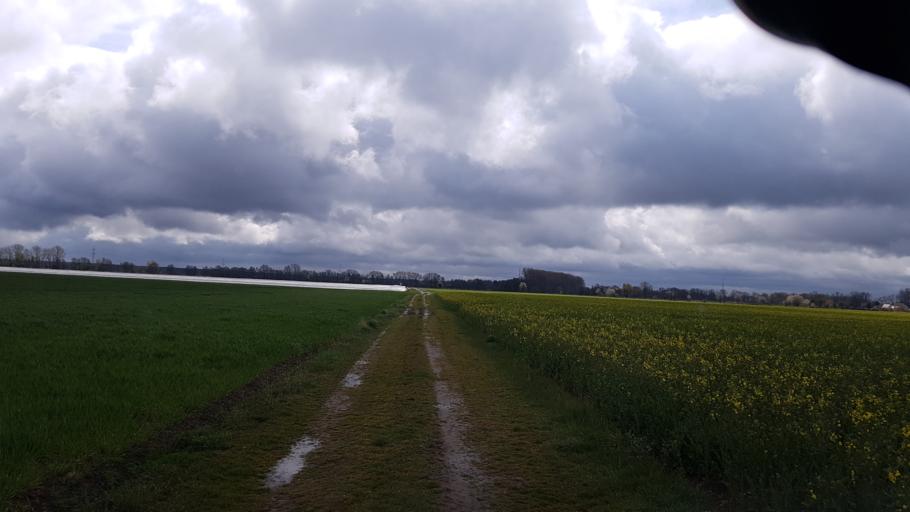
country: DE
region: Brandenburg
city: Doberlug-Kirchhain
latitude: 51.6588
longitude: 13.5514
